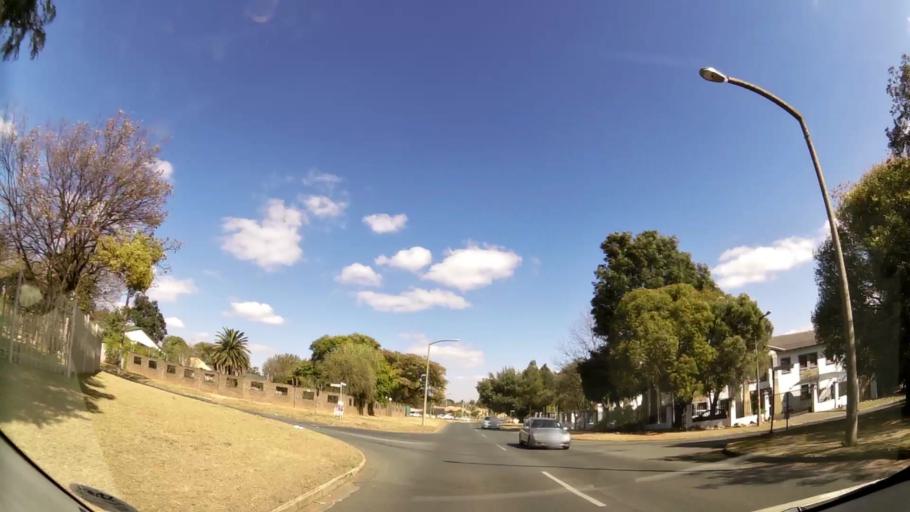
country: ZA
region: Gauteng
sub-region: West Rand District Municipality
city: Krugersdorp
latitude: -26.0900
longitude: 27.7879
